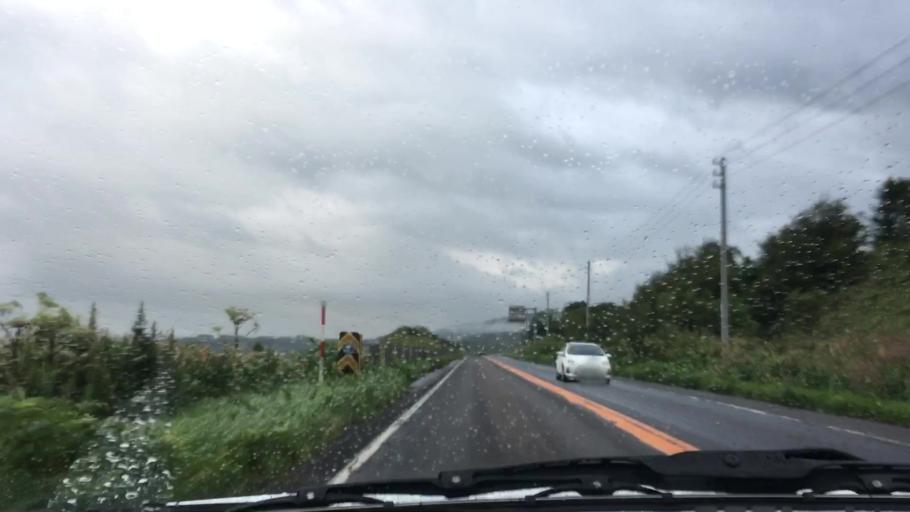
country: JP
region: Hokkaido
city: Nanae
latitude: 42.1863
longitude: 140.4364
